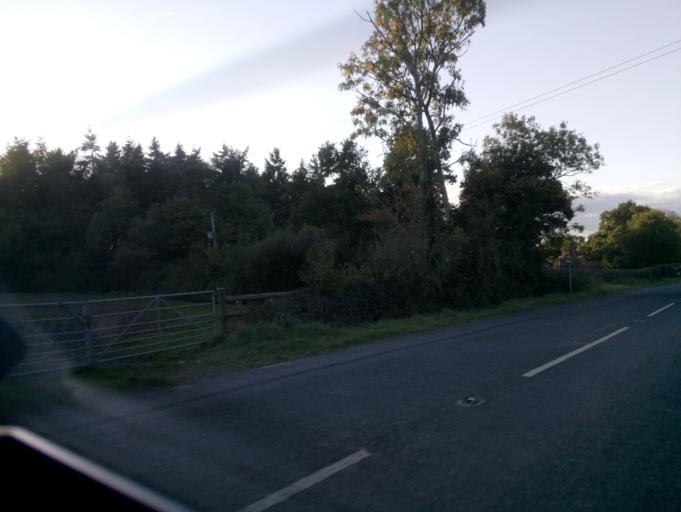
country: GB
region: England
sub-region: Worcestershire
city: Upton upon Severn
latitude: 52.0017
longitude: -2.2357
